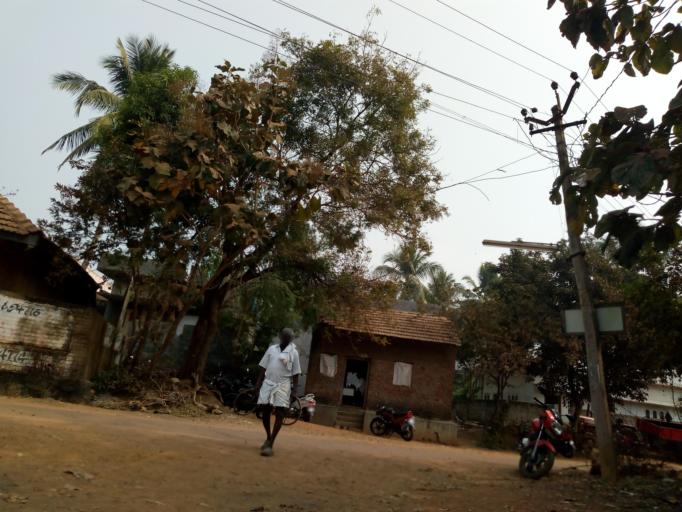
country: IN
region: Andhra Pradesh
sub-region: West Godavari
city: Tadepallegudem
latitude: 16.8748
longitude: 81.3174
